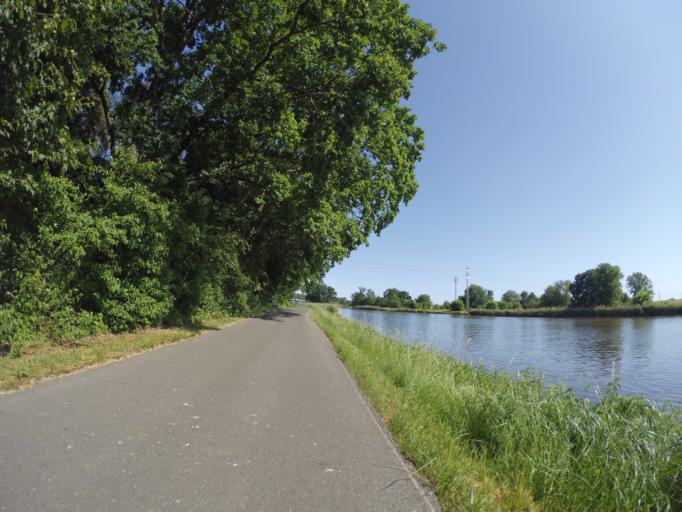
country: CZ
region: Central Bohemia
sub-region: Okres Nymburk
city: Nymburk
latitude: 50.1692
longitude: 15.0792
